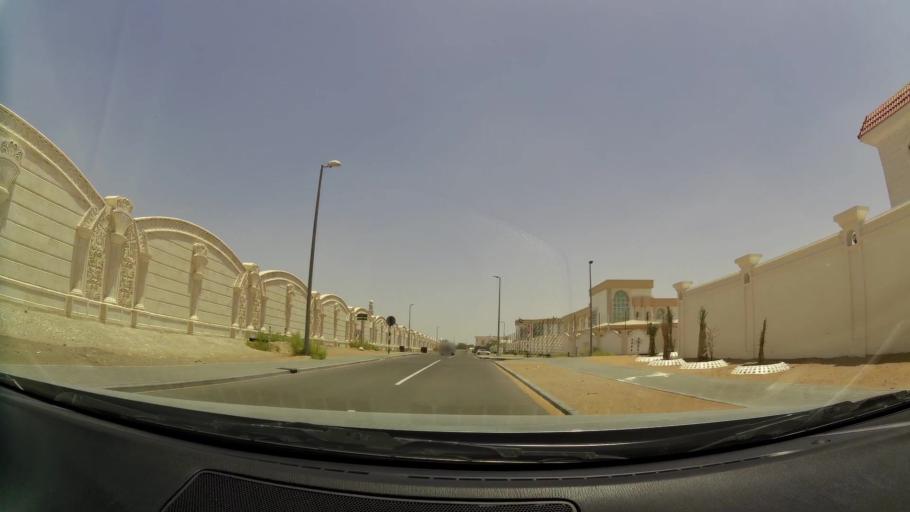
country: OM
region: Al Buraimi
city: Al Buraymi
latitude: 24.2708
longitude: 55.7151
